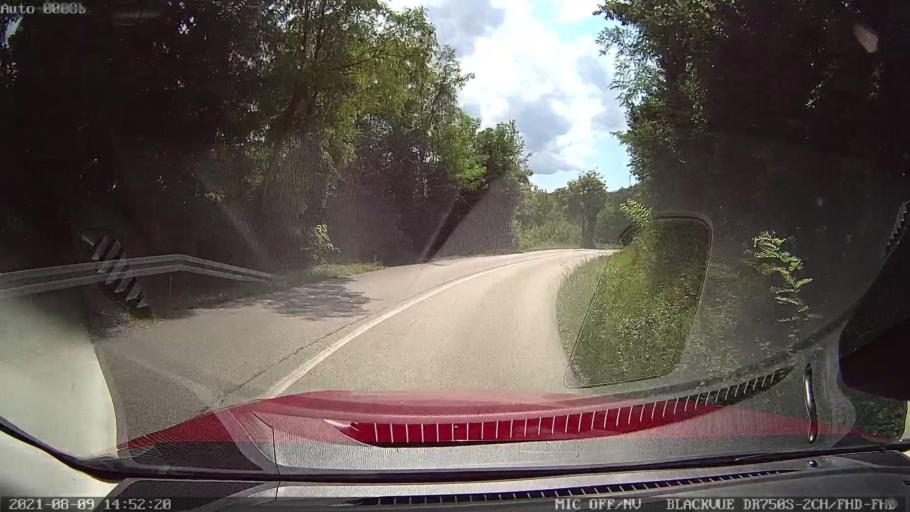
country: HR
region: Istarska
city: Pazin
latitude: 45.2889
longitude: 14.0838
